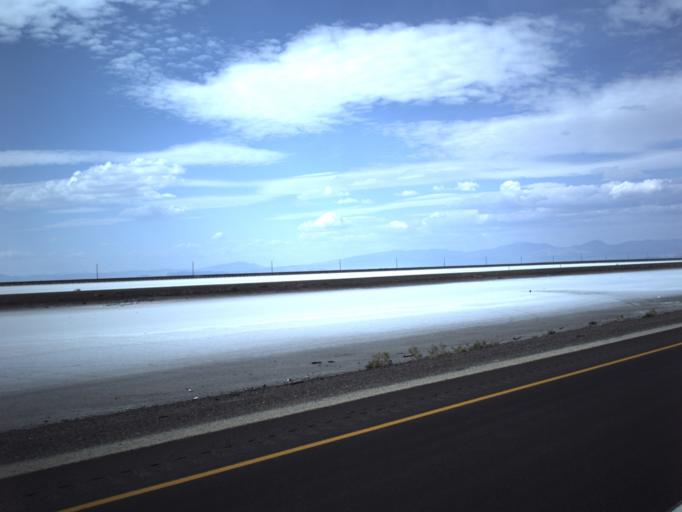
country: US
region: Utah
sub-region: Tooele County
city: Wendover
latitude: 40.7349
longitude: -113.6352
